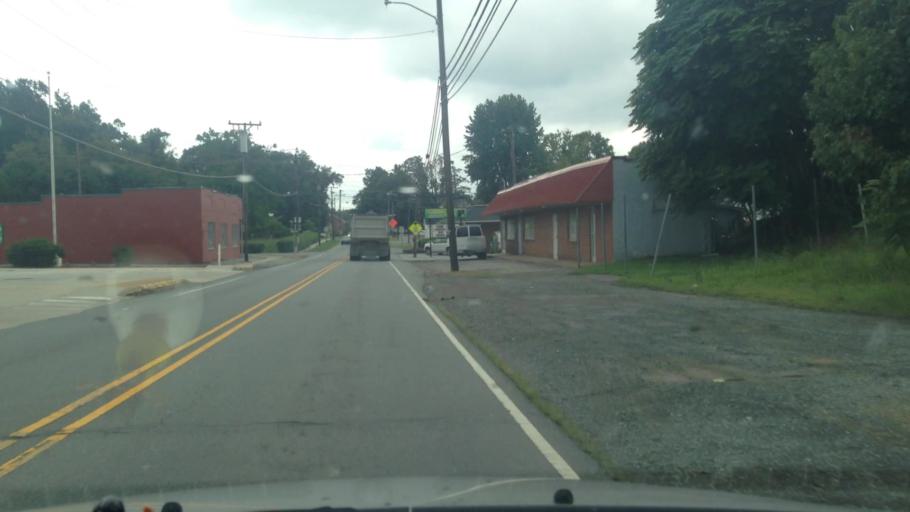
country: US
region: North Carolina
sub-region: Forsyth County
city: Walkertown
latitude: 36.1764
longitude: -80.1530
